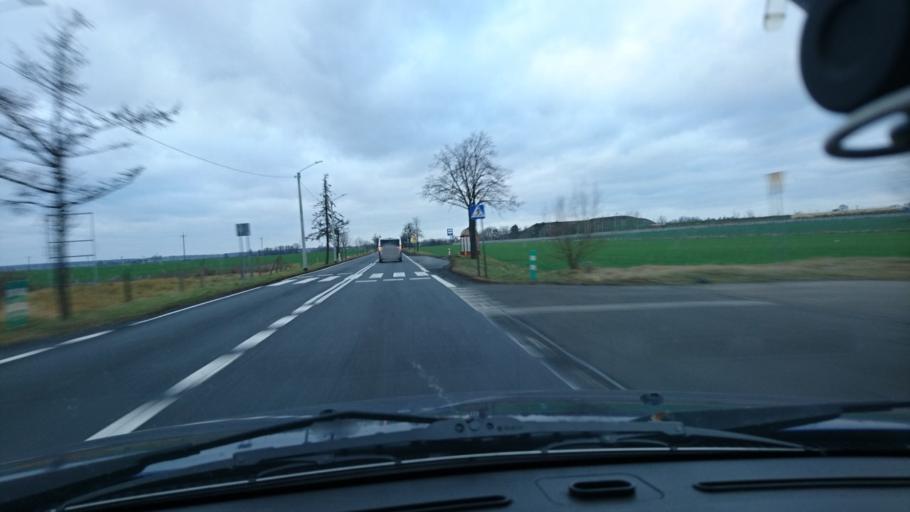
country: PL
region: Opole Voivodeship
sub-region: Powiat kluczborski
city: Kluczbork
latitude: 50.9963
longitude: 18.2083
